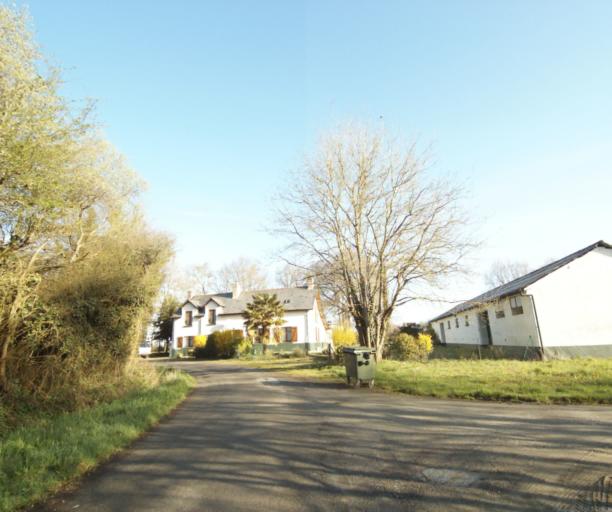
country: FR
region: Pays de la Loire
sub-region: Departement de la Loire-Atlantique
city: Bouvron
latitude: 47.4101
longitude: -1.8266
